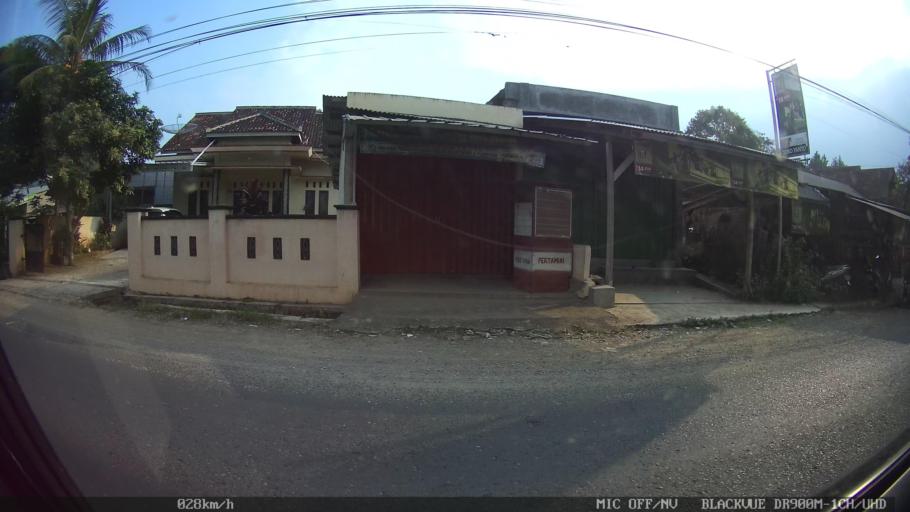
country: ID
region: Lampung
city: Natar
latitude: -5.3684
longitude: 105.1715
